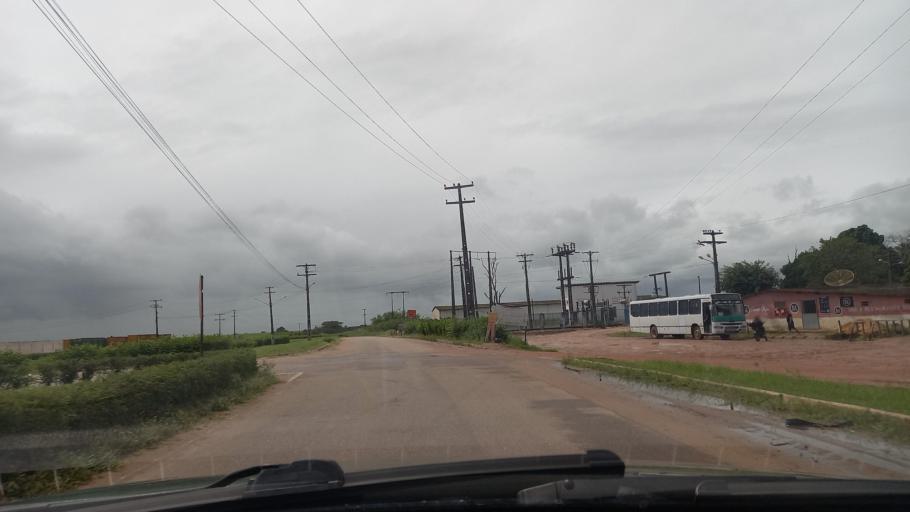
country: BR
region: Alagoas
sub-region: Sao Miguel Dos Campos
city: Sao Miguel dos Campos
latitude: -9.8076
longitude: -36.2097
